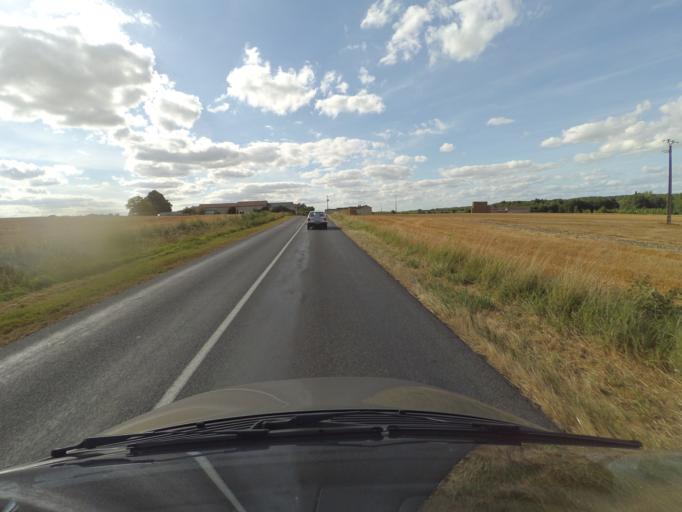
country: FR
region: Poitou-Charentes
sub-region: Departement de la Vienne
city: Saint-Gervais-les-Trois-Clochers
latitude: 46.9544
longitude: 0.4025
